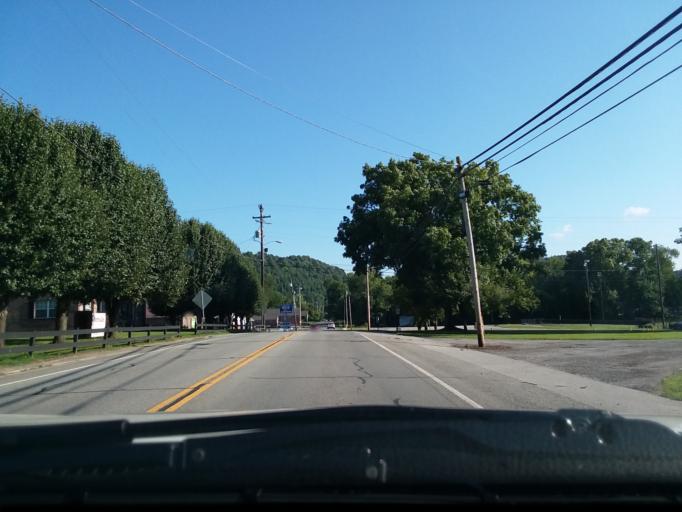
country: US
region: Tennessee
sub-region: Clay County
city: Celina
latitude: 36.5465
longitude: -85.5056
